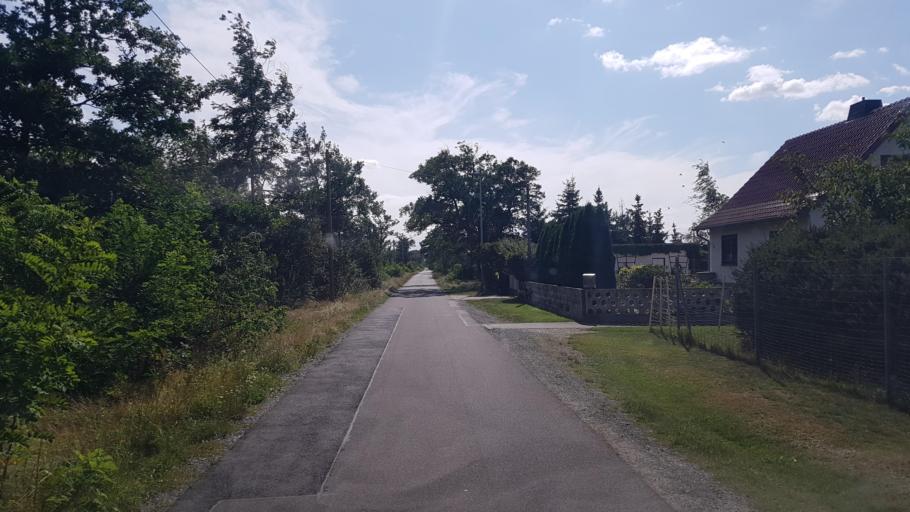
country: DE
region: Brandenburg
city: Muhlberg
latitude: 51.4534
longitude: 13.2983
